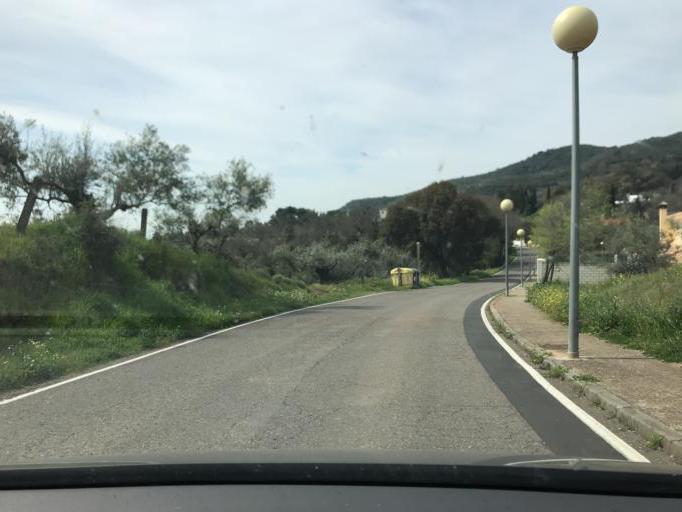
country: ES
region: Andalusia
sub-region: Province of Cordoba
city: Cordoba
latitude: 37.9301
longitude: -4.8035
